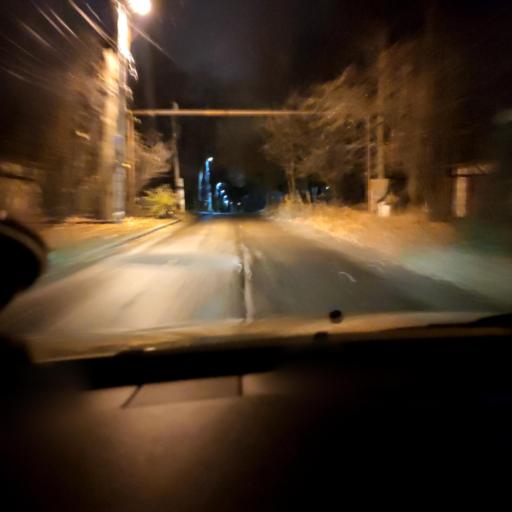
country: RU
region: Samara
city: Samara
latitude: 53.2953
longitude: 50.2005
